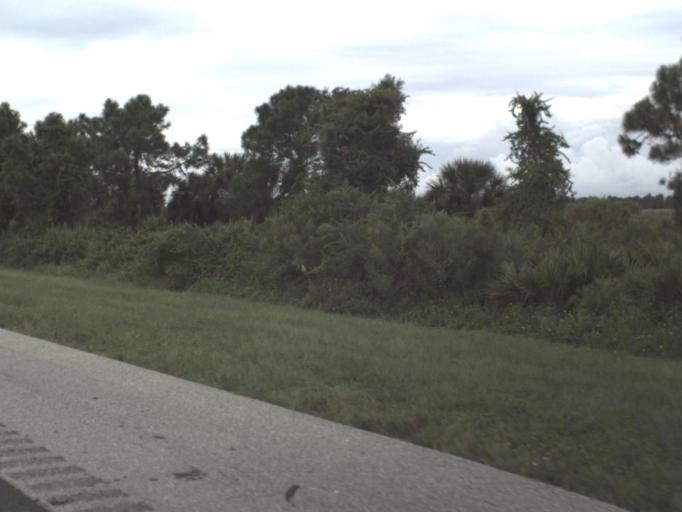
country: US
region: Florida
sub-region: Sarasota County
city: Osprey
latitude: 27.2033
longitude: -82.4421
